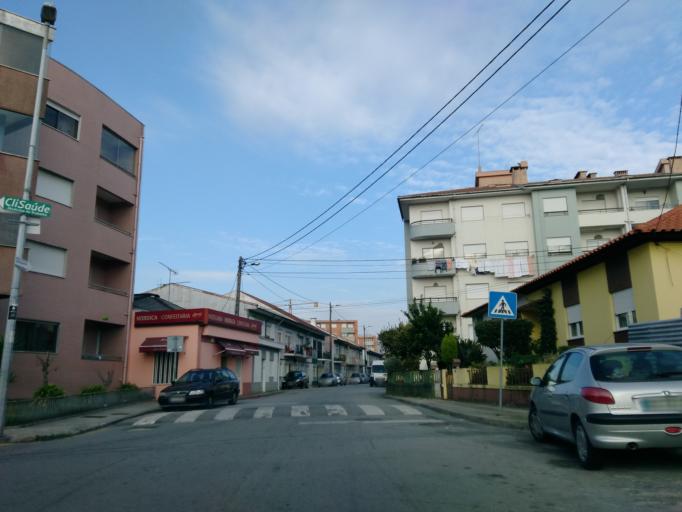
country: PT
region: Braga
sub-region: Braga
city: Braga
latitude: 41.5366
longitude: -8.4405
